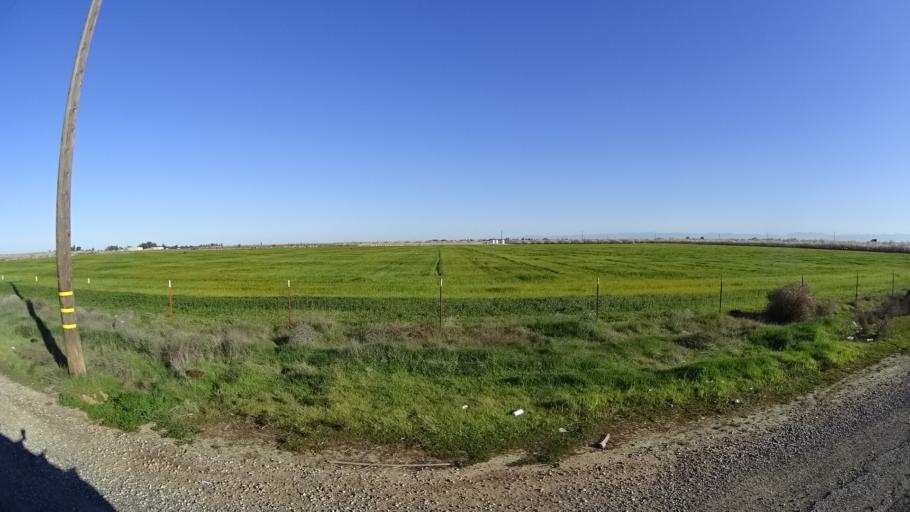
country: US
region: California
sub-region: Fresno County
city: Biola
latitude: 36.7788
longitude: -119.9239
